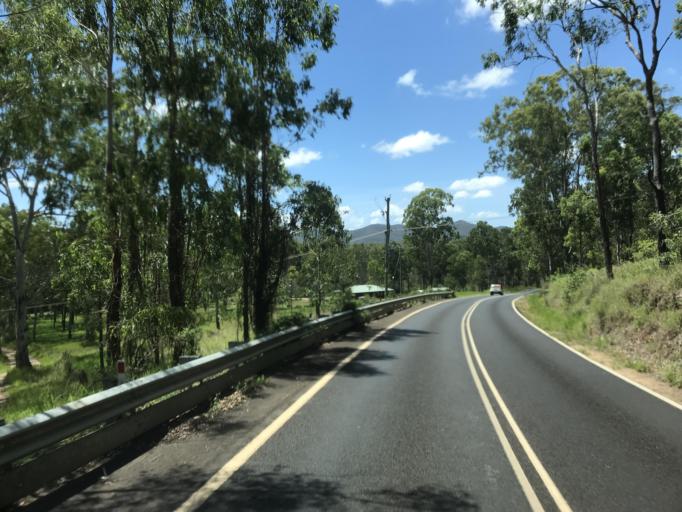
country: AU
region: Queensland
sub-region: Tablelands
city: Atherton
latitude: -17.4209
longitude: 145.3941
